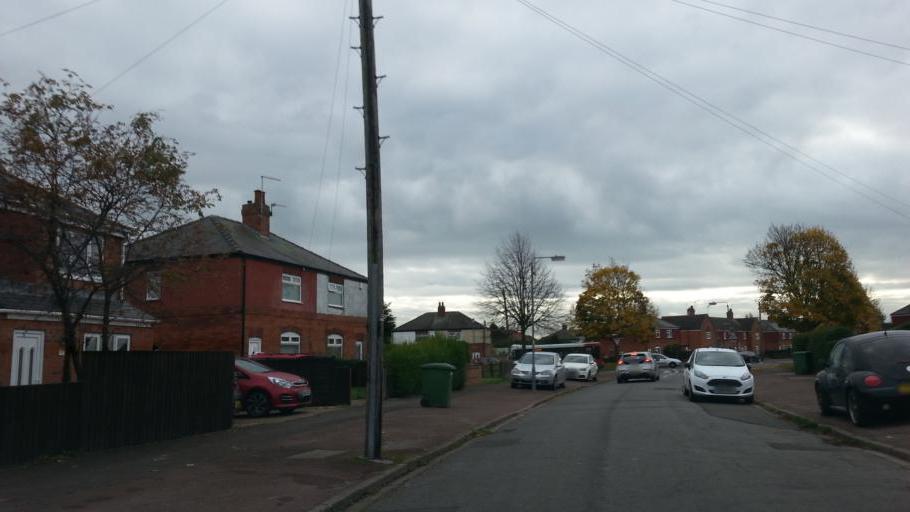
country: GB
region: England
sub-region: Nottinghamshire
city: Newark on Trent
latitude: 53.0645
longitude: -0.8128
